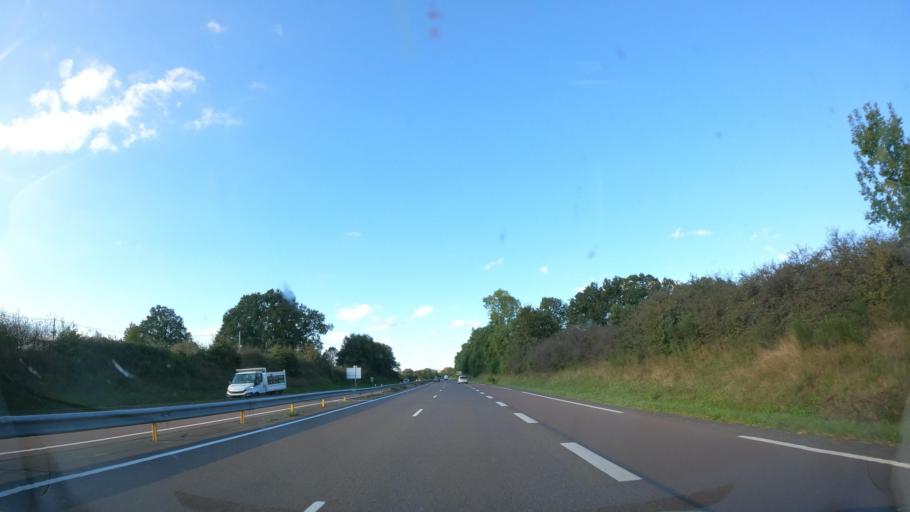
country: FR
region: Bourgogne
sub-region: Departement de Saone-et-Loire
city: Saint-Vallier
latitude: 46.6459
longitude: 4.3297
